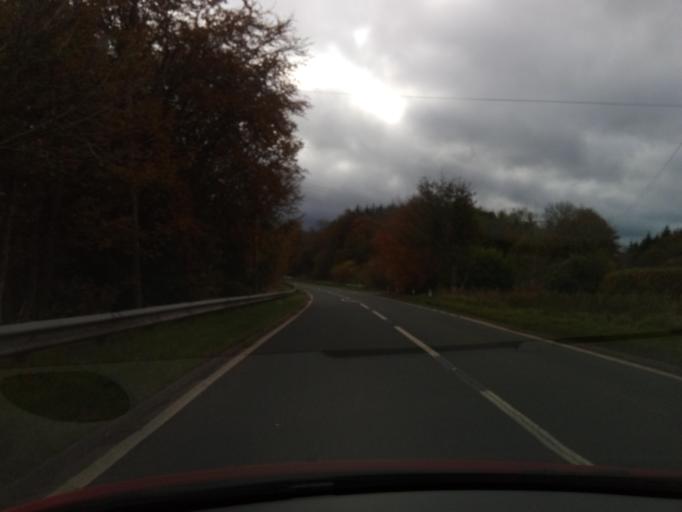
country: GB
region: Scotland
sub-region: The Scottish Borders
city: Jedburgh
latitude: 55.3840
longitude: -2.4965
